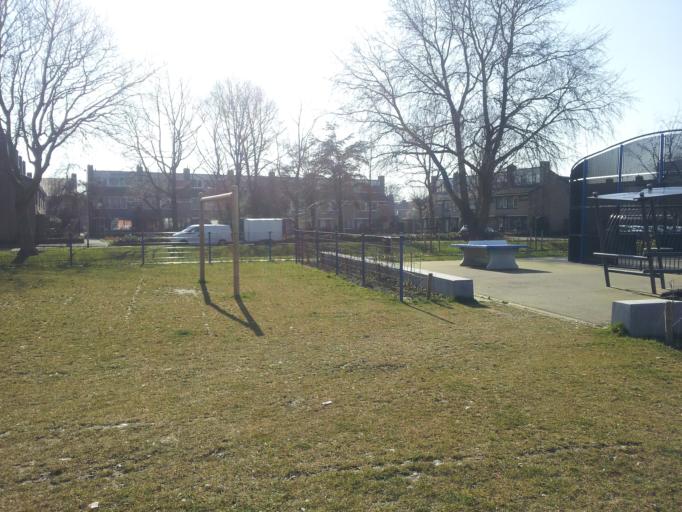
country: NL
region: South Holland
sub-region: Gemeente Lansingerland
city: Bleiswijk
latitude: 52.0092
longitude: 4.5378
